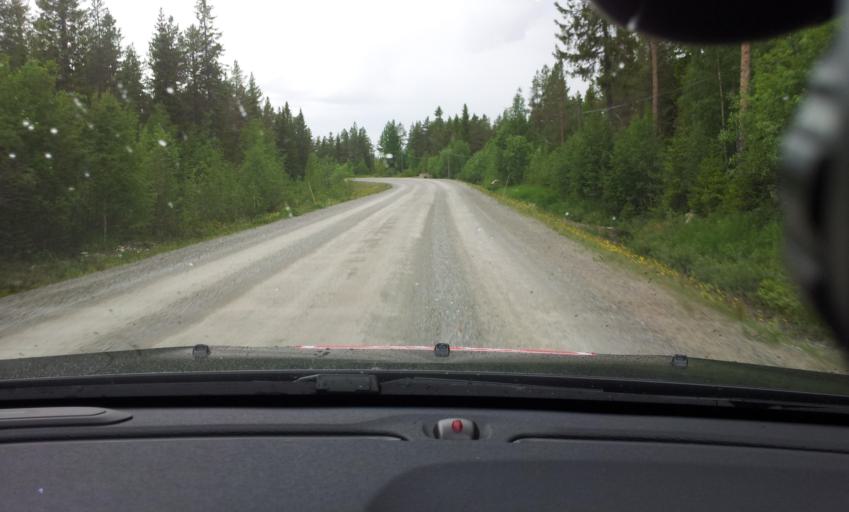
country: SE
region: Jaemtland
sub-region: OEstersunds Kommun
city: Brunflo
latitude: 63.1007
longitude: 15.0588
